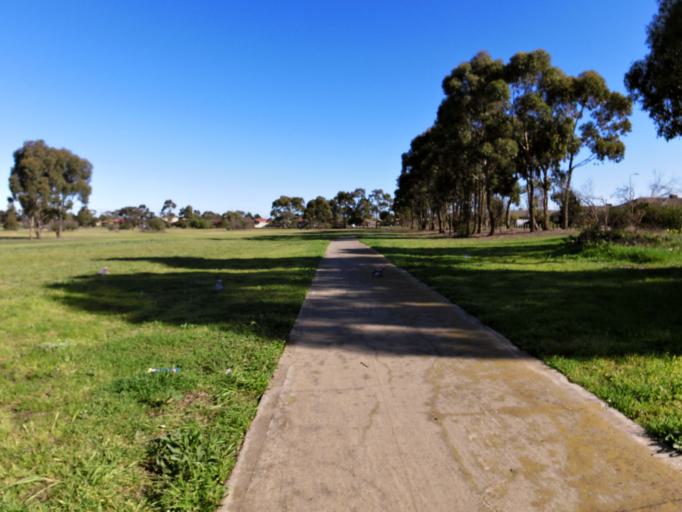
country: AU
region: Victoria
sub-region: Wyndham
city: Tarneit
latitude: -37.8827
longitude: 144.6707
